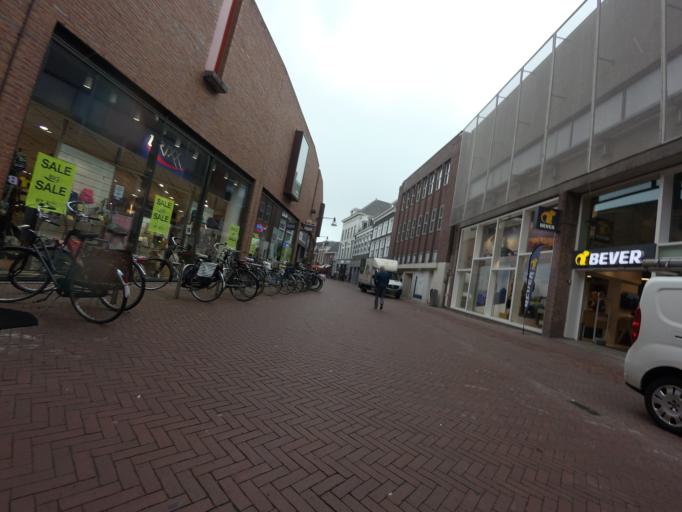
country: NL
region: Friesland
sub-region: Gemeente Leeuwarden
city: Leeuwarden
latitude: 53.1996
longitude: 5.7961
